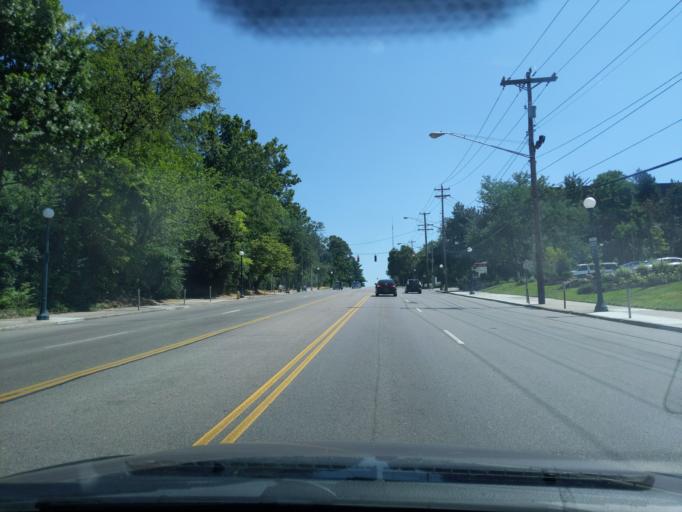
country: US
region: Ohio
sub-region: Hamilton County
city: Saint Bernard
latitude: 39.1398
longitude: -84.5196
